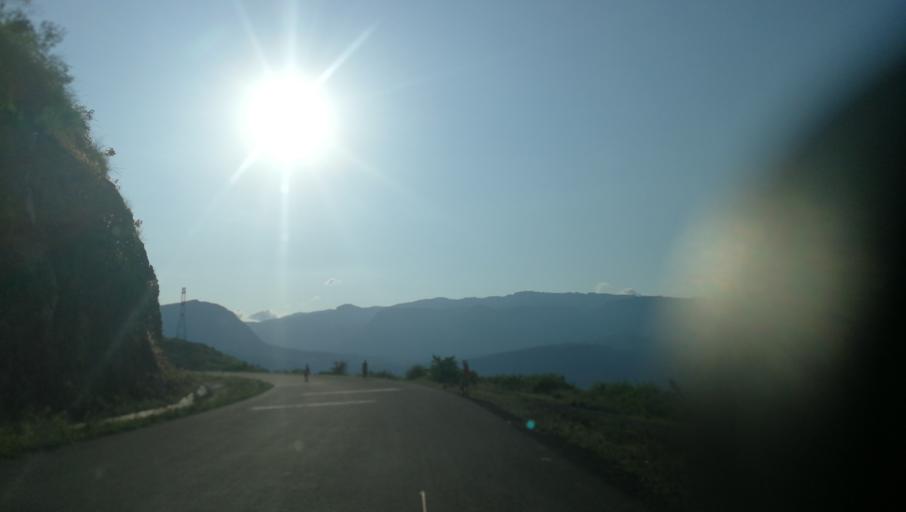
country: ET
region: Southern Nations, Nationalities, and People's Region
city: Areka
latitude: 6.8317
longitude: 37.3123
